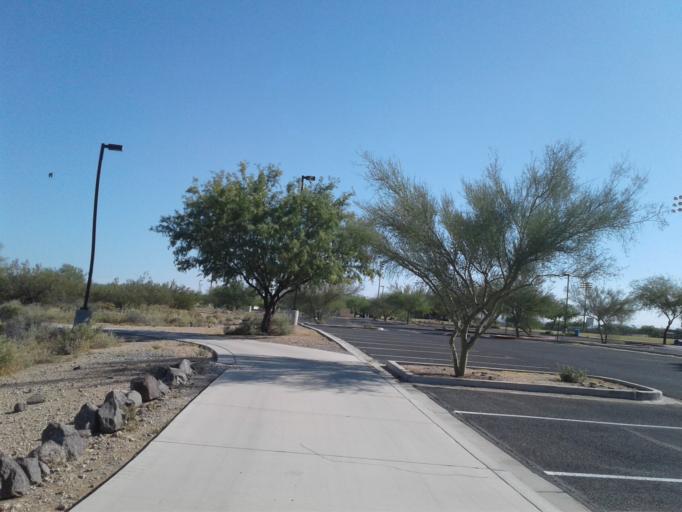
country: US
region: Arizona
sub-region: Maricopa County
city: Cave Creek
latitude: 33.6816
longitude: -112.0246
